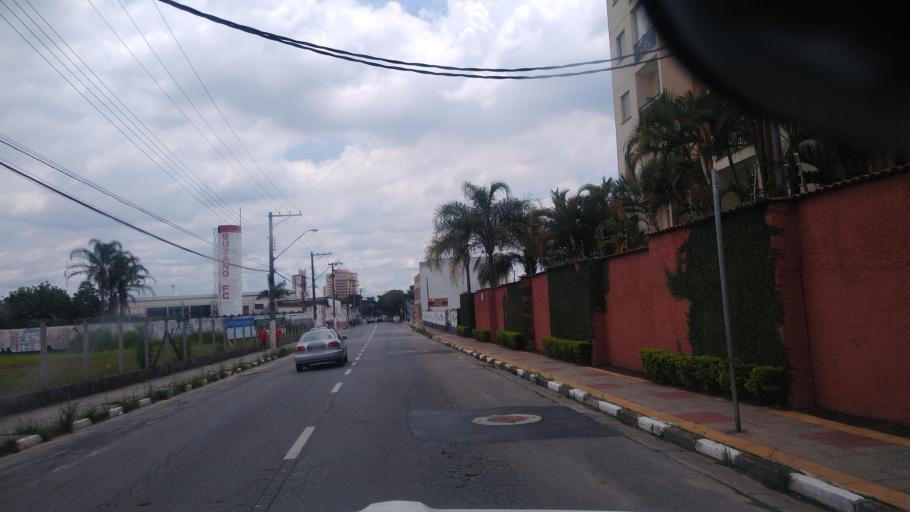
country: BR
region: Sao Paulo
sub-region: Suzano
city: Suzano
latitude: -23.5485
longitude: -46.3165
